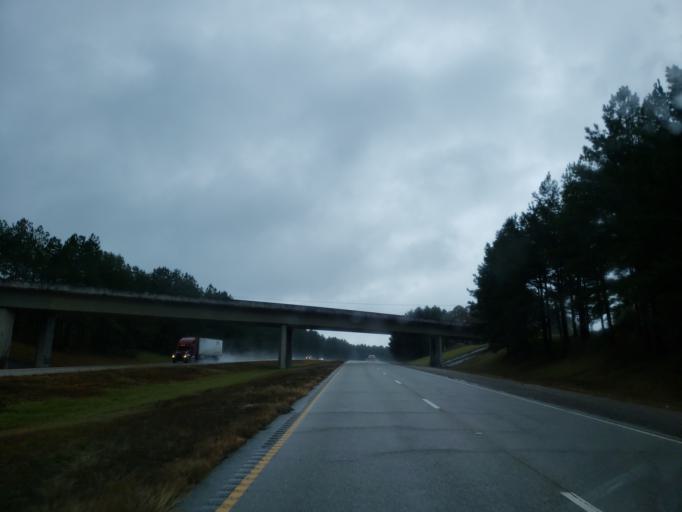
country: US
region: Mississippi
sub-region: Lauderdale County
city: Meridian
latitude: 32.2799
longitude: -88.6966
